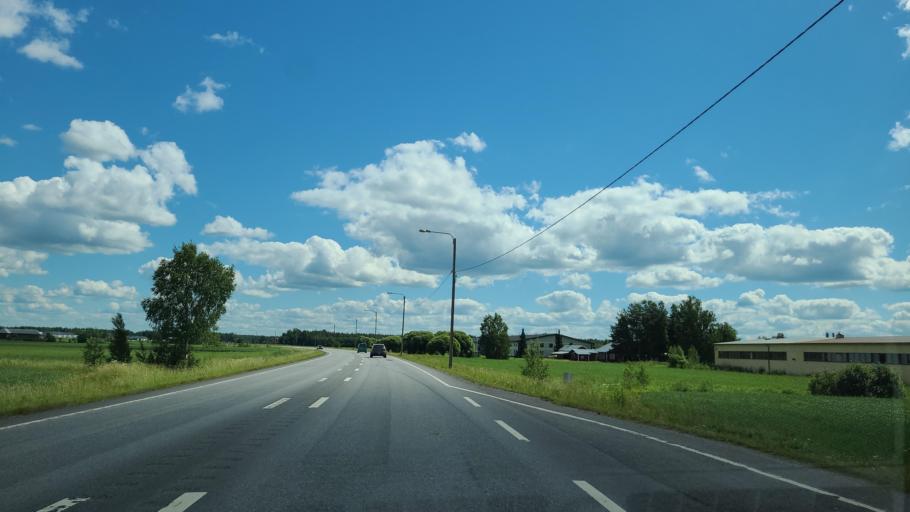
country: FI
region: Southern Ostrobothnia
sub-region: Seinaejoki
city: Ylistaro
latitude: 62.9345
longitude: 22.4843
